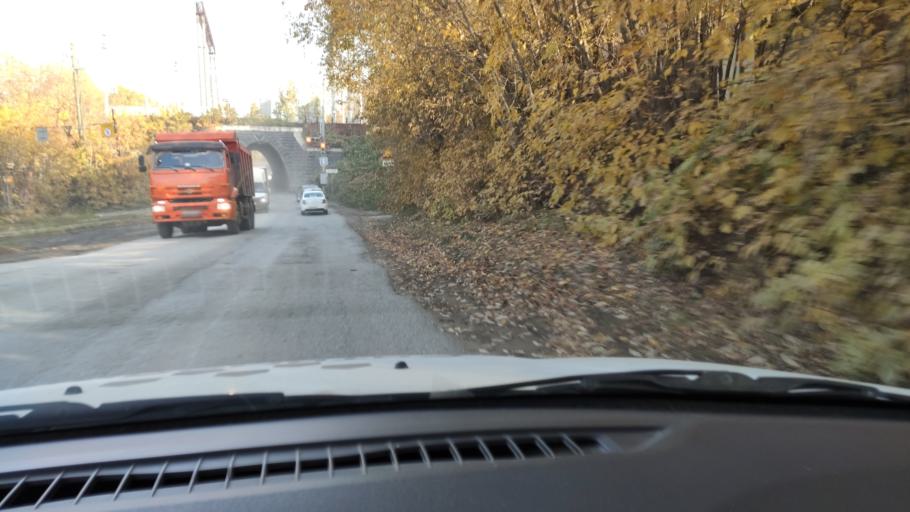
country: RU
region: Perm
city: Kondratovo
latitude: 58.0042
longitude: 56.1630
